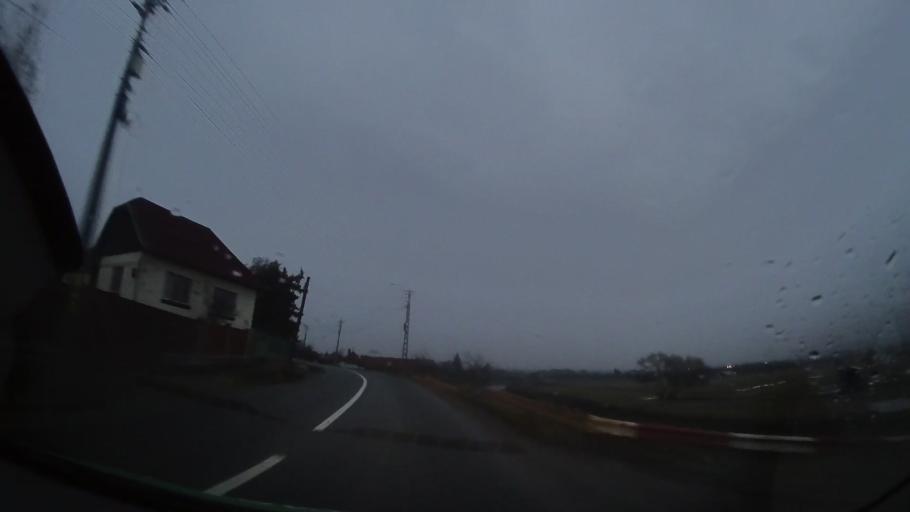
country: RO
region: Harghita
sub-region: Comuna Remetea
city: Remetea
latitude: 46.7956
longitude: 25.4564
